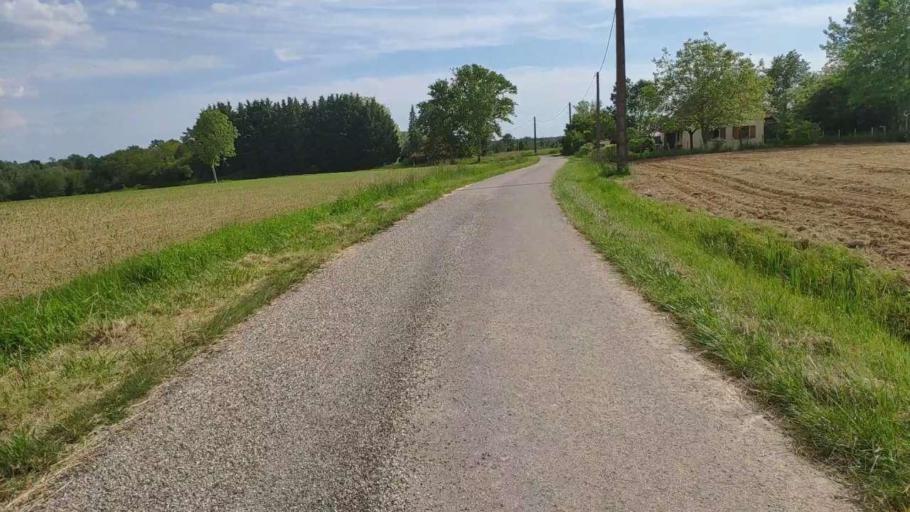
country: FR
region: Franche-Comte
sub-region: Departement du Jura
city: Bletterans
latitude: 46.8121
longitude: 5.3857
